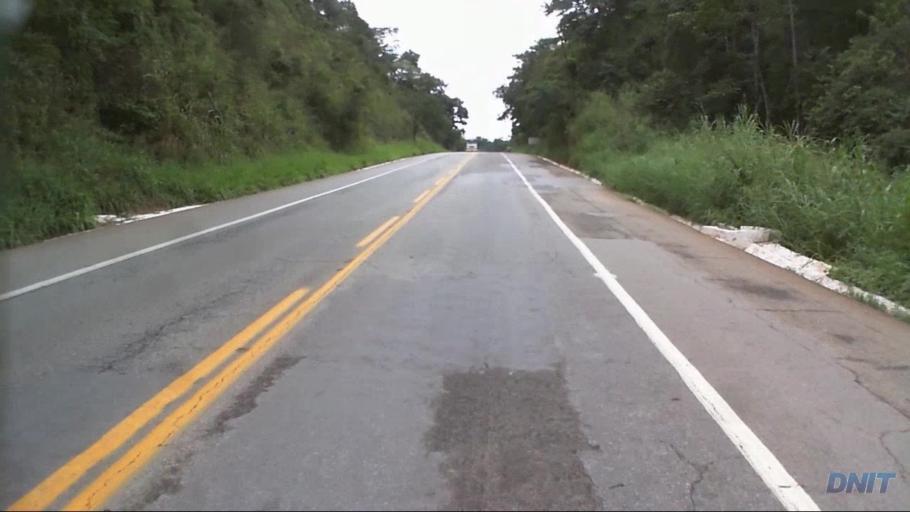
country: BR
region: Minas Gerais
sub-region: Barao De Cocais
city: Barao de Cocais
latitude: -19.8080
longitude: -43.4014
